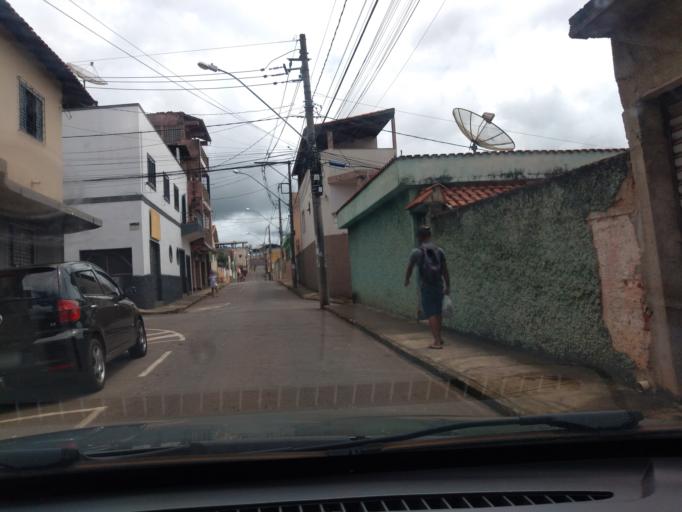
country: BR
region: Minas Gerais
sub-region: Tres Coracoes
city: Tres Coracoes
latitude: -21.6919
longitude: -45.2538
